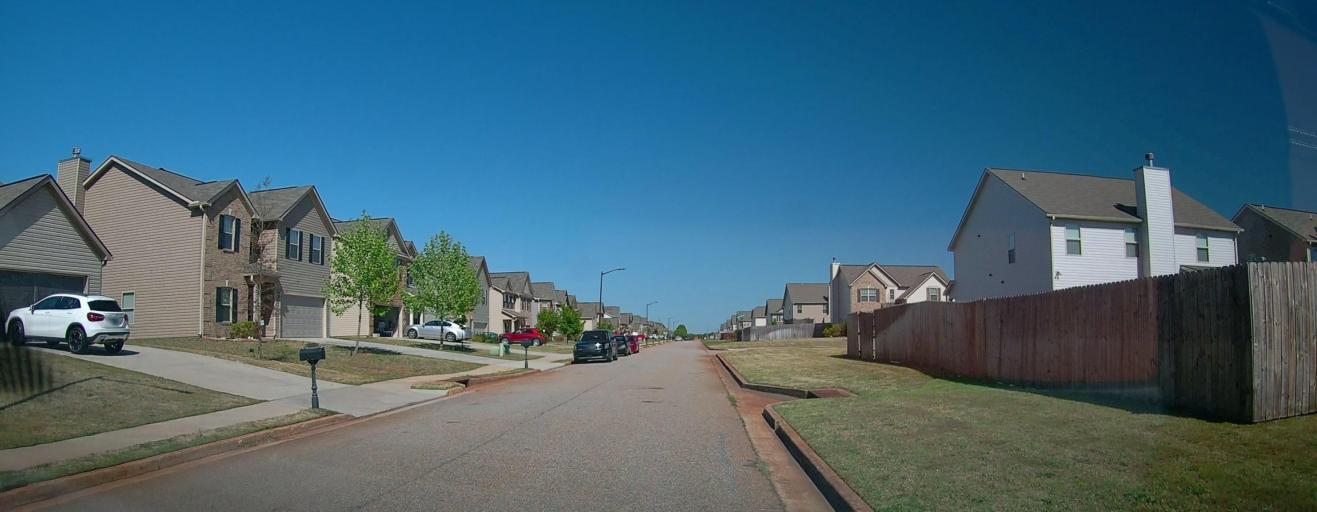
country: US
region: Georgia
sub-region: Houston County
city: Centerville
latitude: 32.6449
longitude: -83.7174
